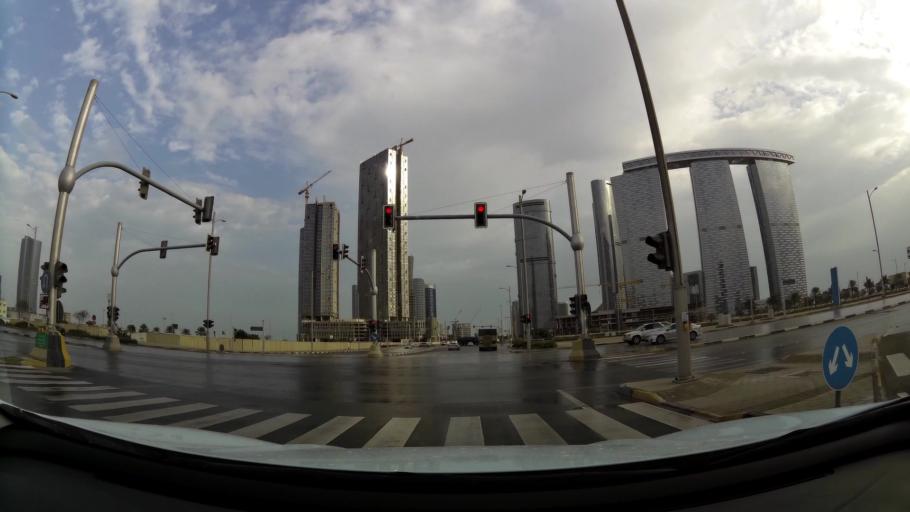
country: AE
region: Abu Dhabi
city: Abu Dhabi
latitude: 24.4899
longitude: 54.4036
